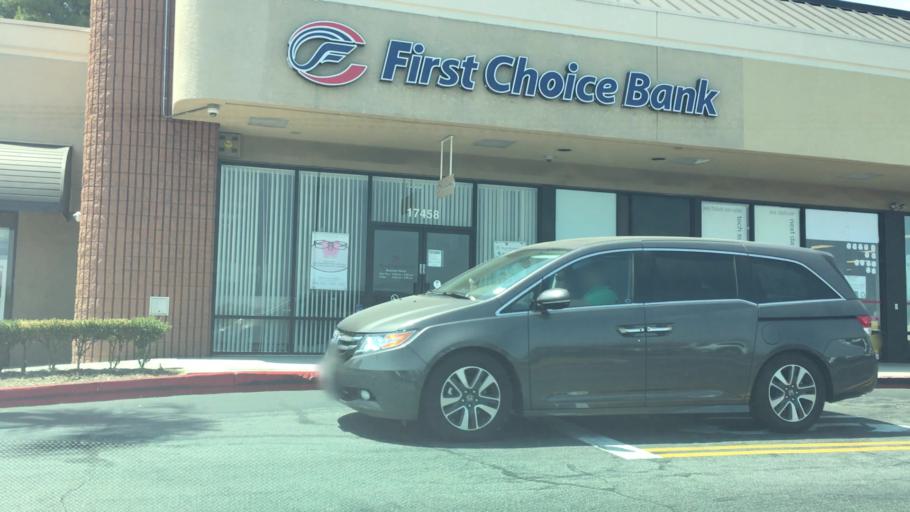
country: US
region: California
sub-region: Los Angeles County
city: Rowland Heights
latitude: 33.9900
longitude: -117.9253
